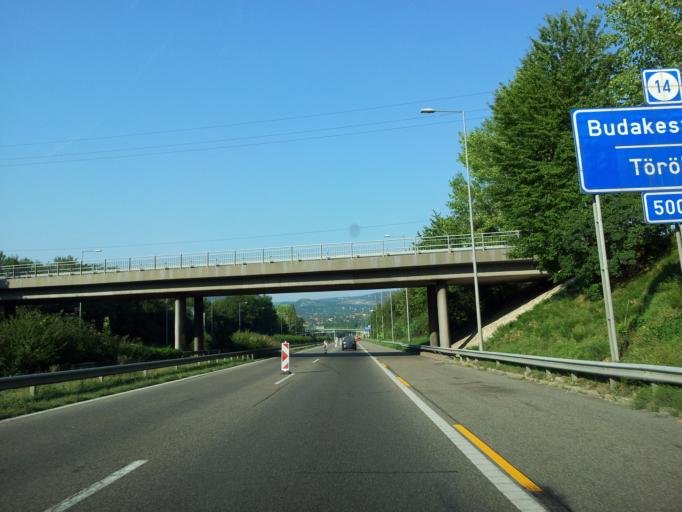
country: HU
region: Pest
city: Toeroekbalint
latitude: 47.4402
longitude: 18.9037
